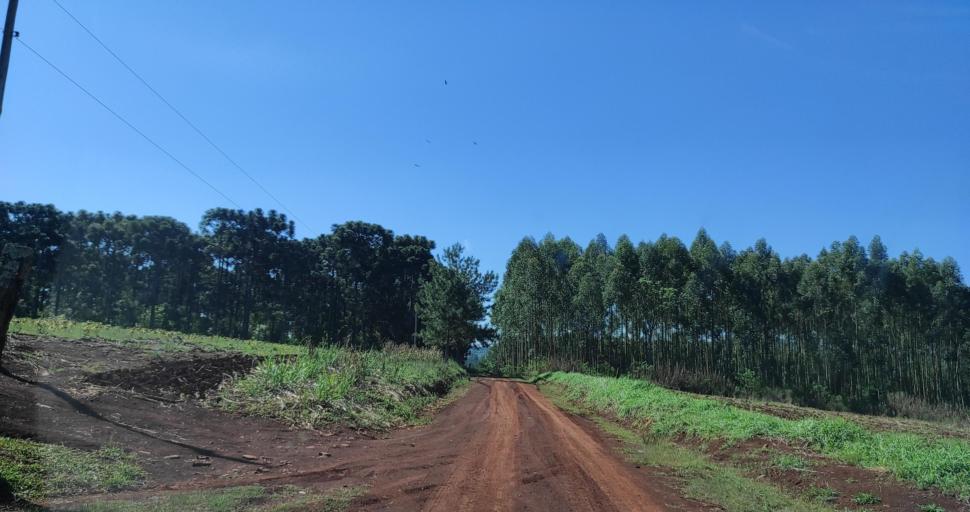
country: AR
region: Misiones
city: Capiovi
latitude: -26.9355
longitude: -55.0016
